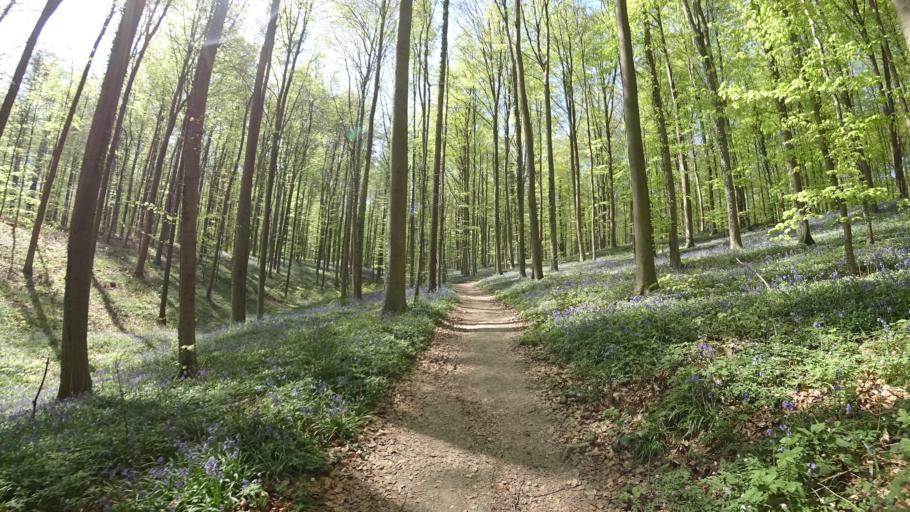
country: BE
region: Wallonia
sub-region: Province du Brabant Wallon
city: Braine-le-Chateau
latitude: 50.7065
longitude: 4.3064
